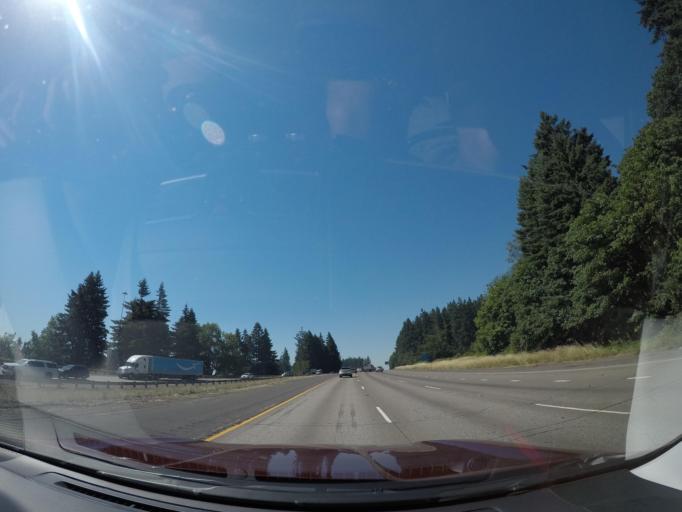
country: US
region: Oregon
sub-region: Clackamas County
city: Wilsonville
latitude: 45.2746
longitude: -122.7775
